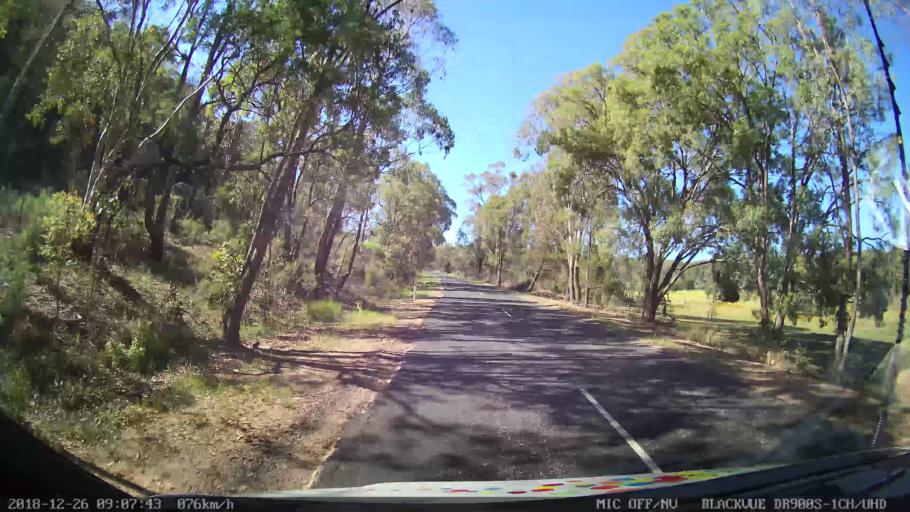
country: AU
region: New South Wales
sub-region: Mid-Western Regional
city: Kandos
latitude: -32.7086
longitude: 150.0031
